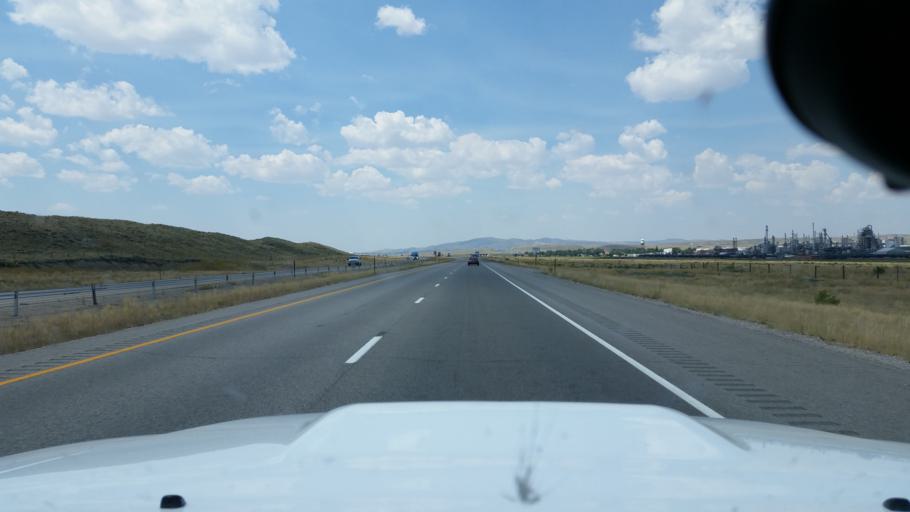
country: US
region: Wyoming
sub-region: Carbon County
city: Rawlins
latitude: 41.7726
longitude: -107.0939
